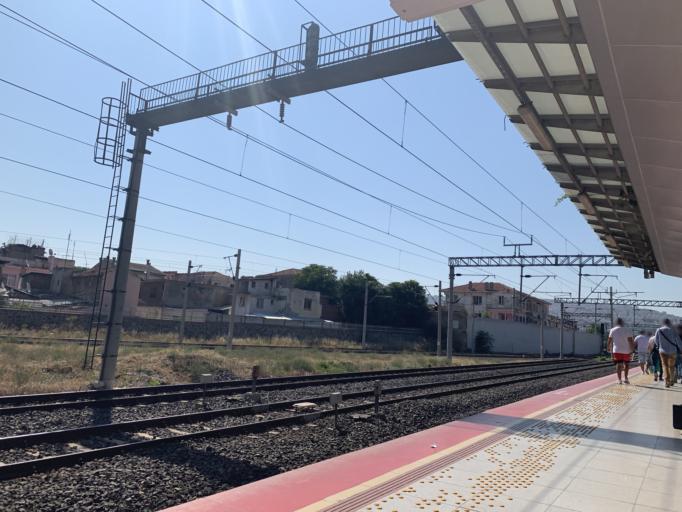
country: TR
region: Izmir
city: Izmir
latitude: 38.4258
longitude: 27.1544
